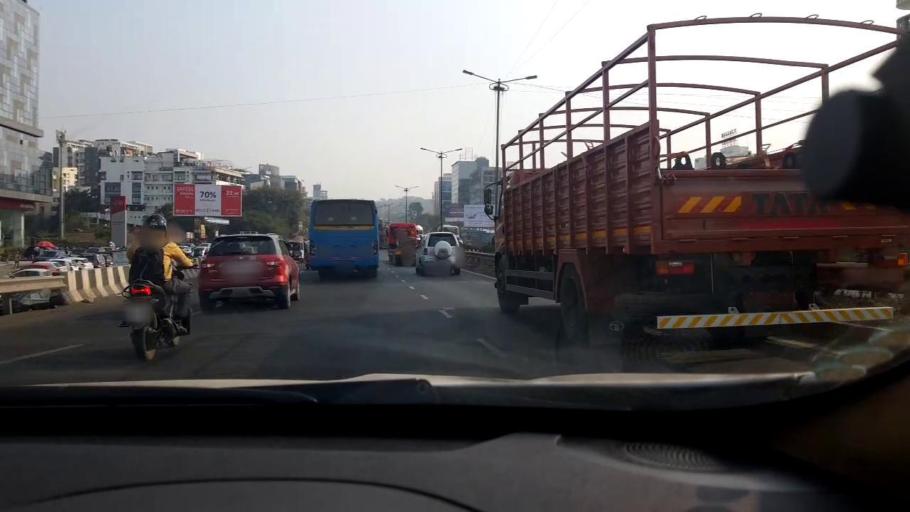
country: IN
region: Maharashtra
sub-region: Pune Division
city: Pimpri
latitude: 18.5577
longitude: 73.7699
